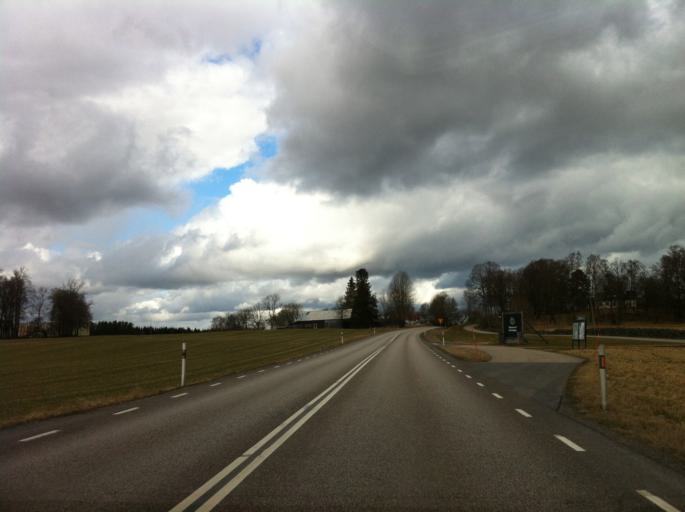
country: SE
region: Vaestra Goetaland
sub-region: Tranemo Kommun
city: Limmared
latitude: 57.6295
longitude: 13.4471
